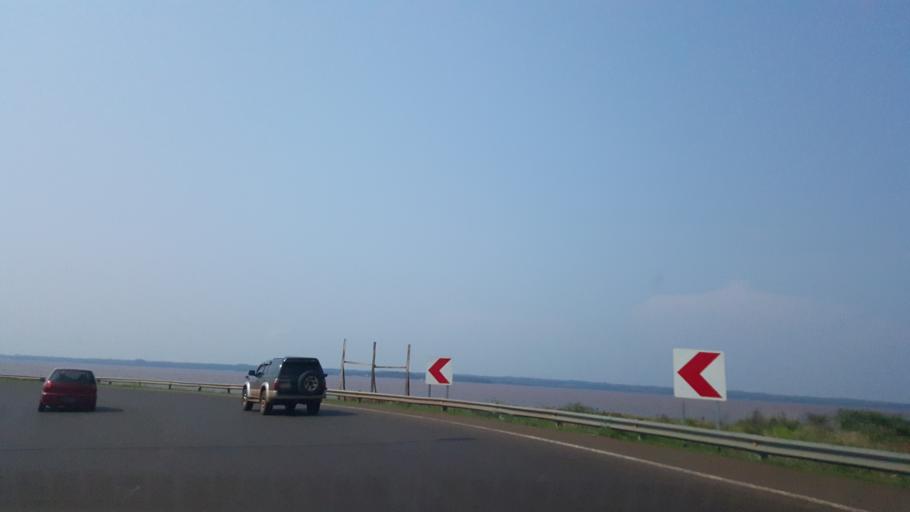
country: AR
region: Misiones
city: Garupa
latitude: -27.4445
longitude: -55.8476
